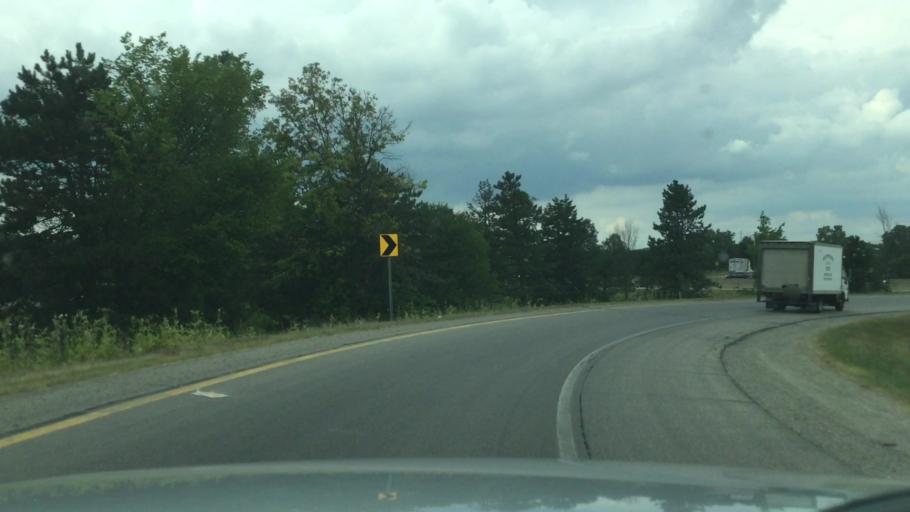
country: US
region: Michigan
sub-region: Washtenaw County
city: Ann Arbor
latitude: 42.2248
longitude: -83.6873
